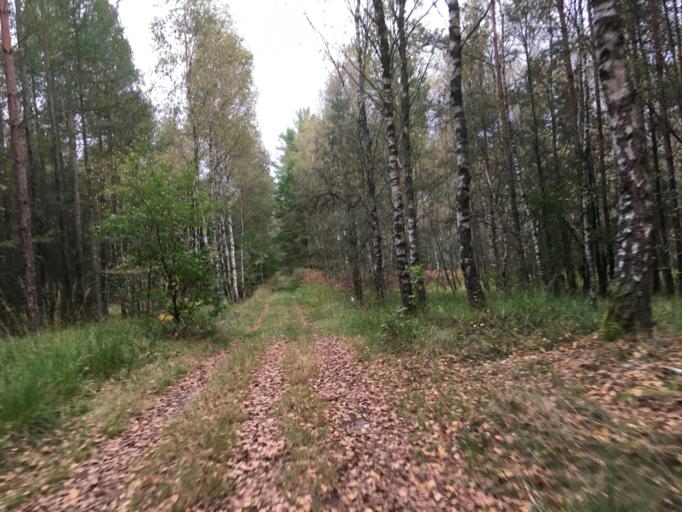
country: DE
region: Brandenburg
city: Birkenwerder
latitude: 52.6966
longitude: 13.3483
